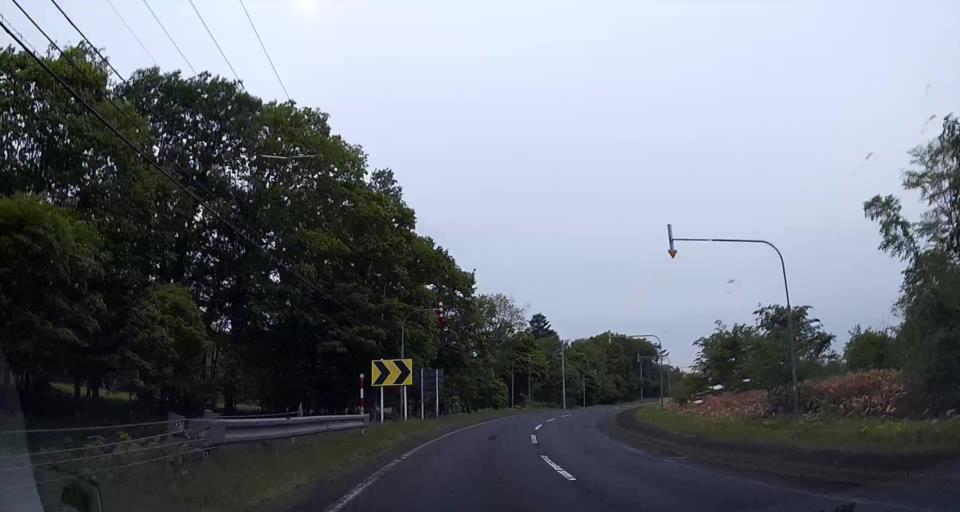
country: JP
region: Hokkaido
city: Shiraoi
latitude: 42.6077
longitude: 141.2844
